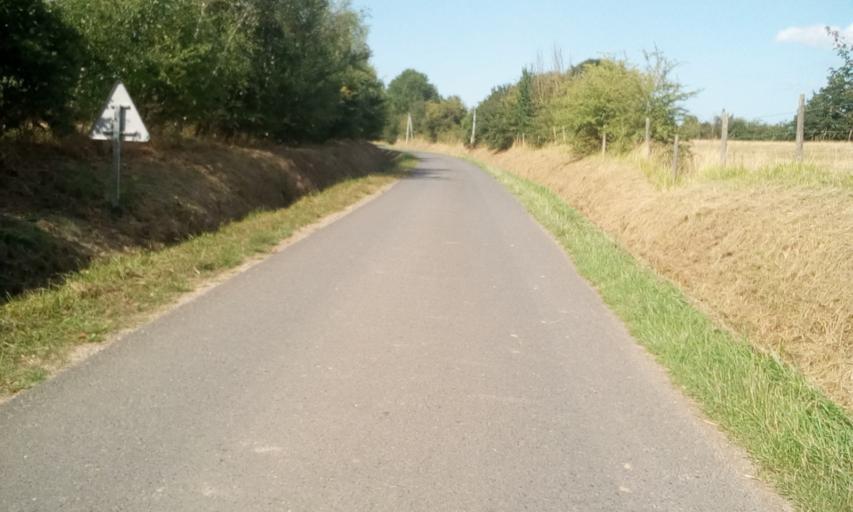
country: FR
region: Lower Normandy
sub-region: Departement du Calvados
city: Argences
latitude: 49.1513
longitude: -0.1245
